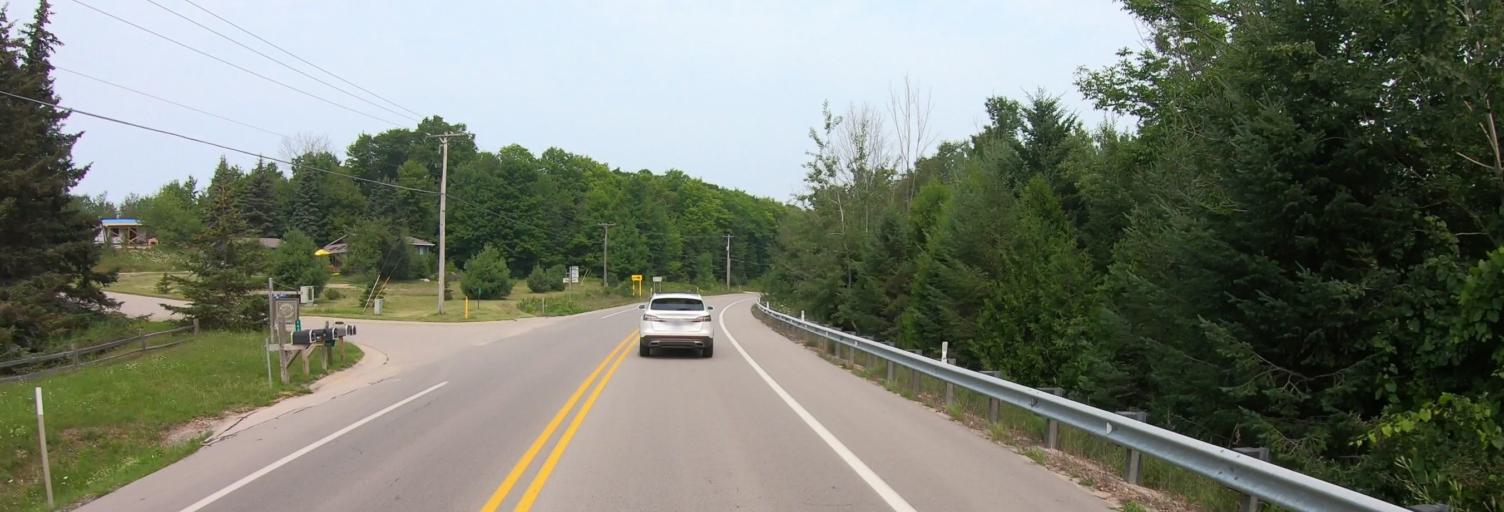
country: US
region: Michigan
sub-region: Leelanau County
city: Leland
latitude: 44.9961
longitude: -85.7709
